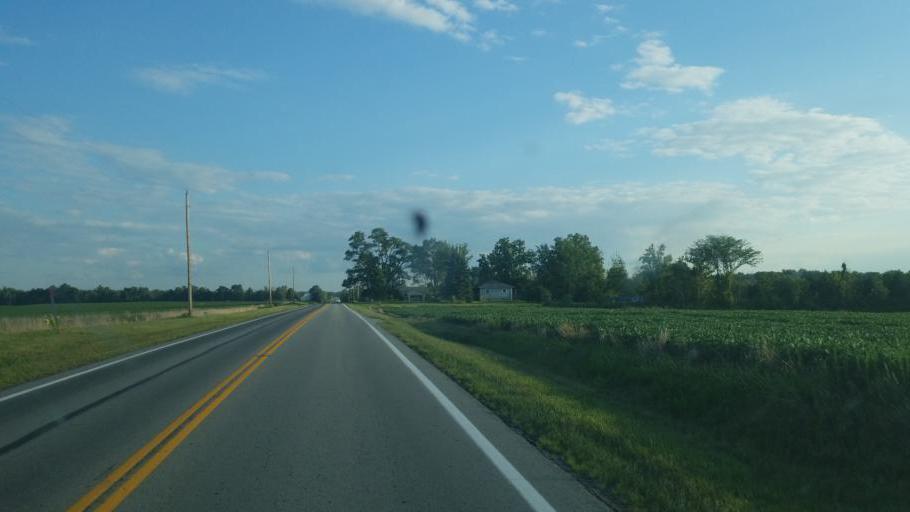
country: US
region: Ohio
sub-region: Huron County
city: Willard
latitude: 41.1020
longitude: -82.7190
